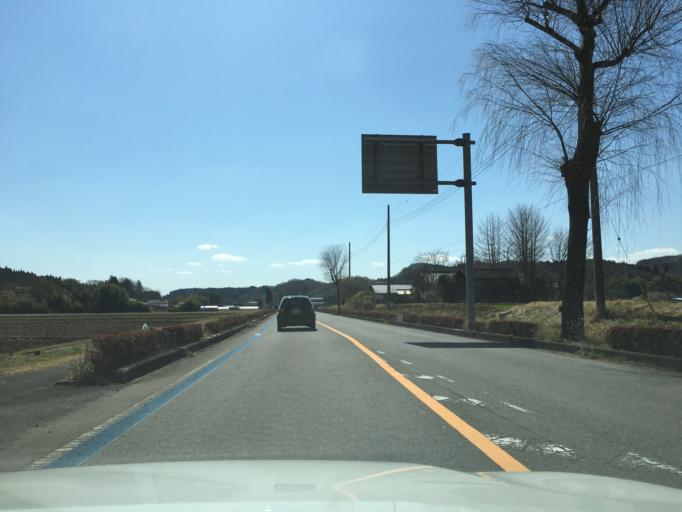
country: JP
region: Tochigi
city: Kuroiso
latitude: 36.9903
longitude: 140.1618
